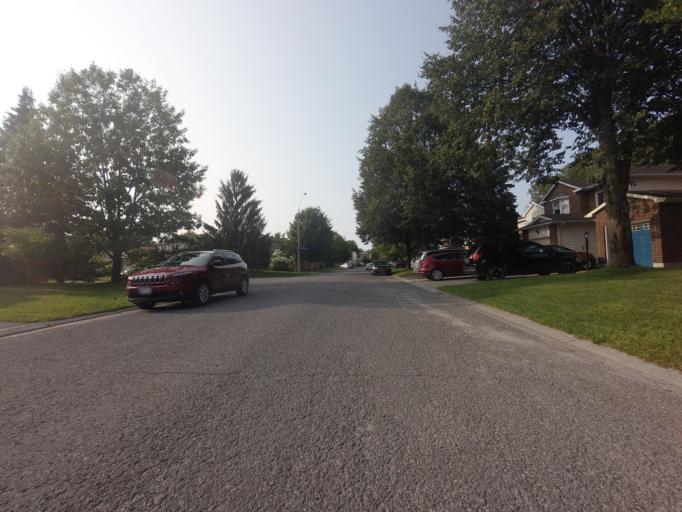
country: CA
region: Ontario
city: Bells Corners
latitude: 45.3384
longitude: -75.7578
